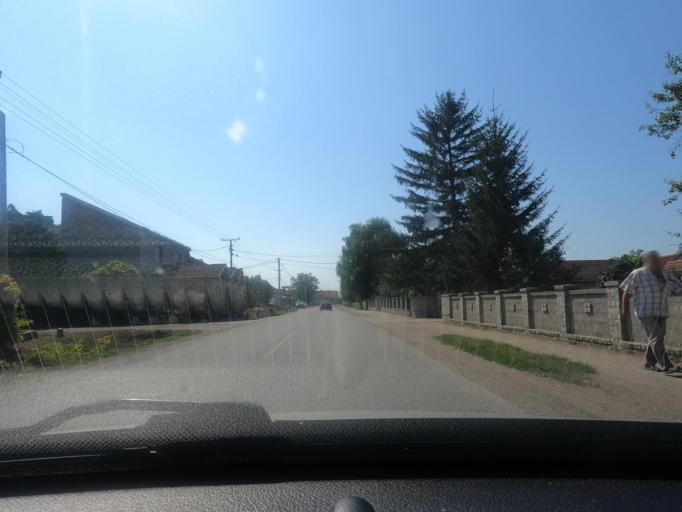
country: RS
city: Lipnicki Sor
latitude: 44.5807
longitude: 19.2628
